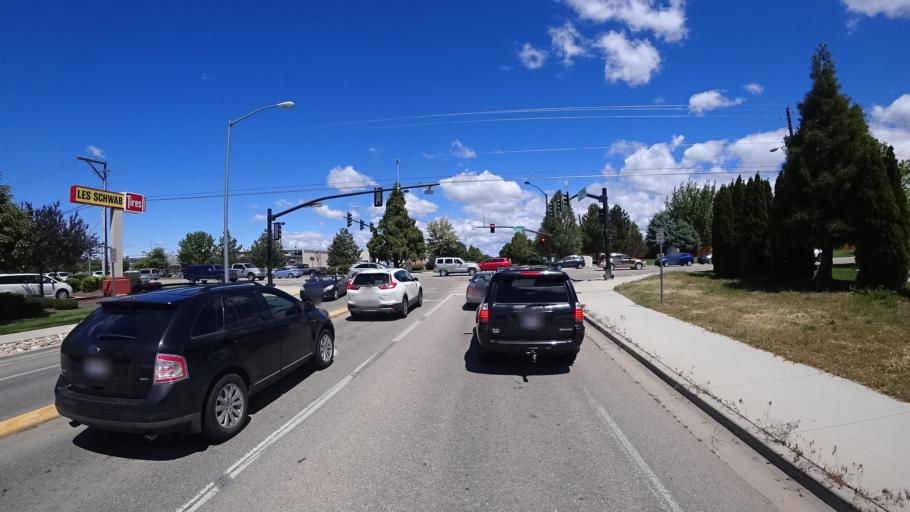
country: US
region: Idaho
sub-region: Ada County
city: Meridian
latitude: 43.6335
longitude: -116.3496
